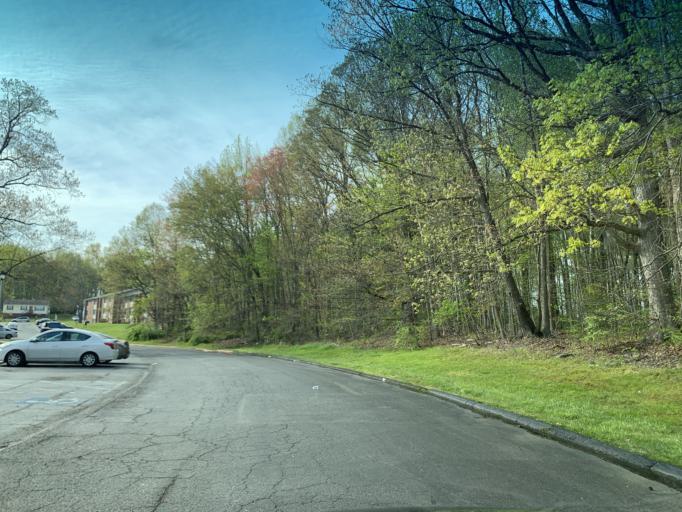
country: US
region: Maryland
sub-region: Harford County
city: Perryman
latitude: 39.4799
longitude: -76.2023
